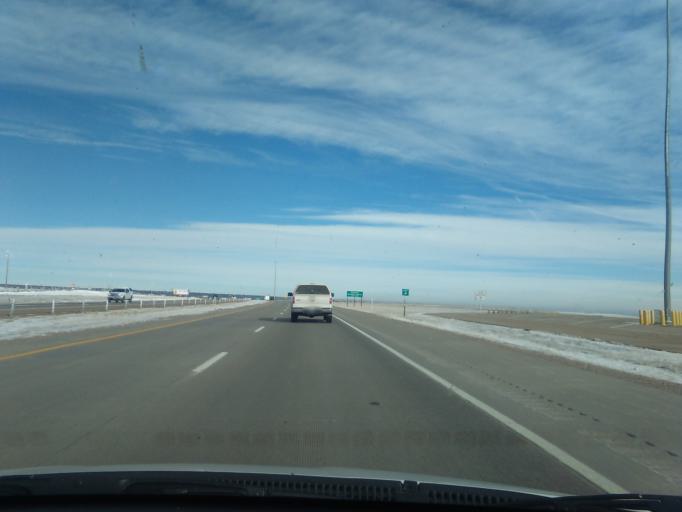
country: US
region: Wyoming
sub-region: Laramie County
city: South Greeley
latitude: 41.0825
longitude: -104.8538
